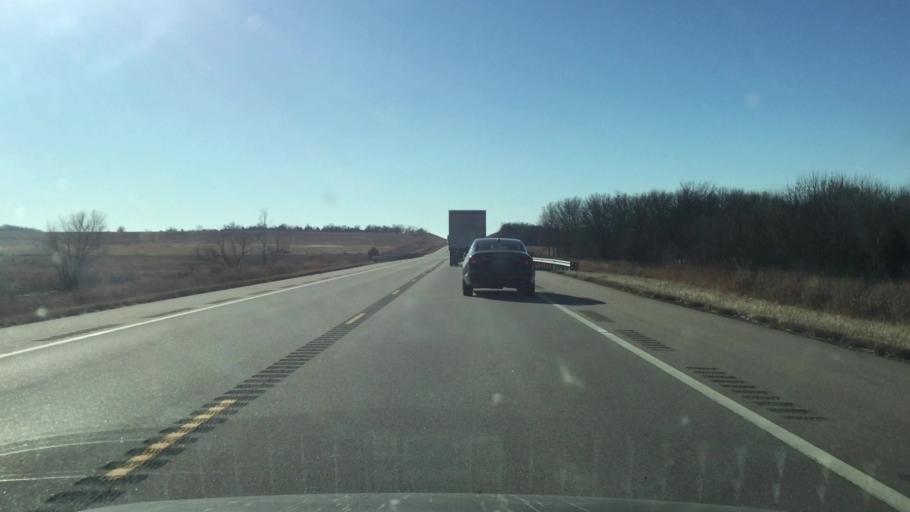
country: US
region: Kansas
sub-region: Allen County
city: Iola
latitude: 38.0215
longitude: -95.3808
